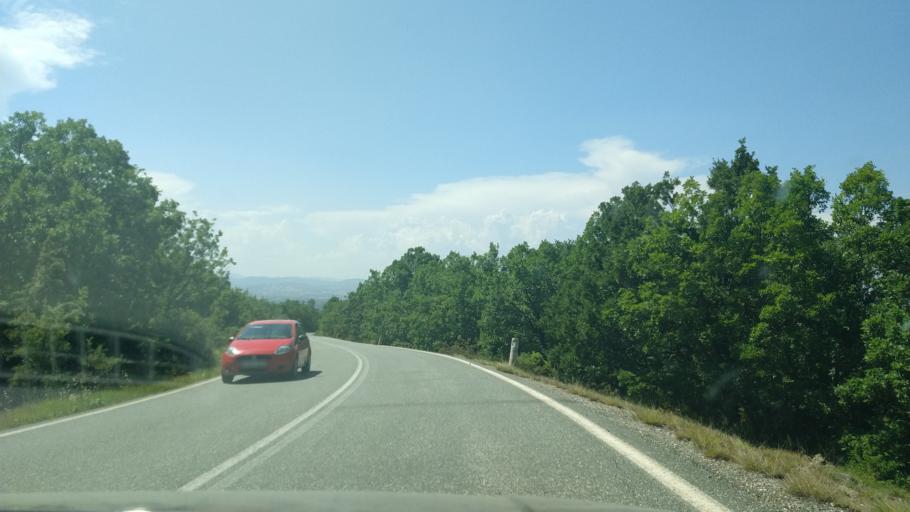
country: GR
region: West Macedonia
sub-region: Nomos Grevenon
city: Grevena
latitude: 40.0209
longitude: 21.4866
